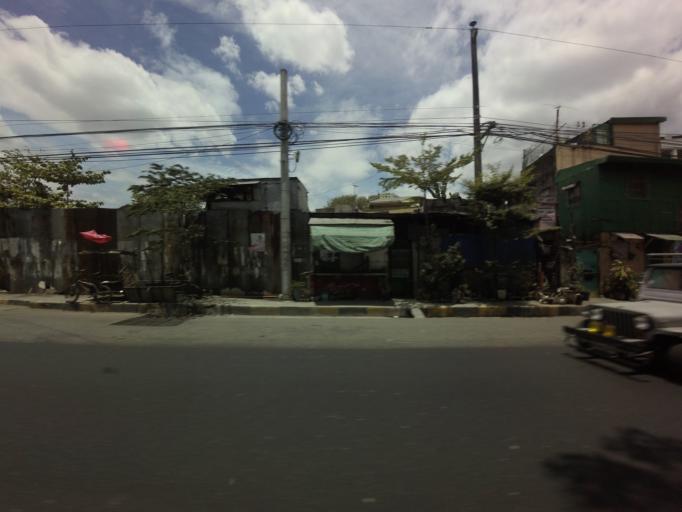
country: PH
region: Metro Manila
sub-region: Marikina
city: Calumpang
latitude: 14.5928
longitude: 121.0927
